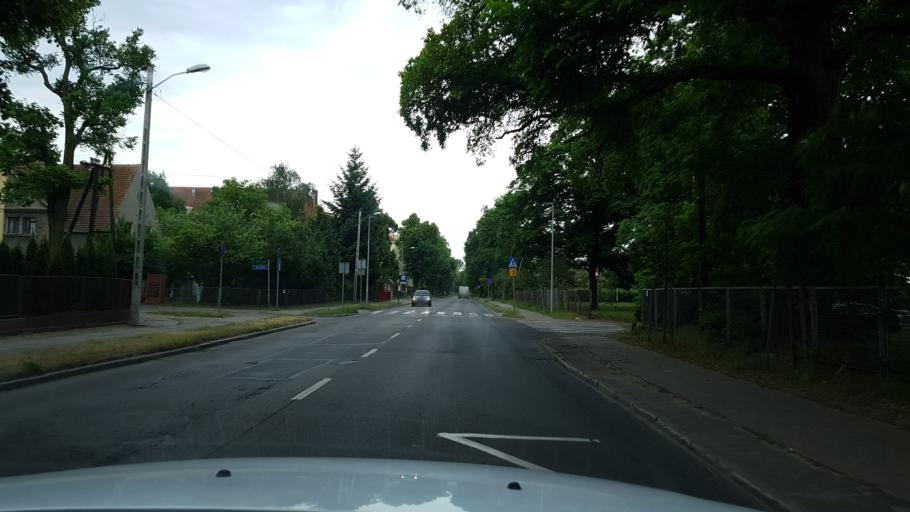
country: PL
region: West Pomeranian Voivodeship
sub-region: Szczecin
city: Szczecin
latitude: 53.3602
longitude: 14.5873
